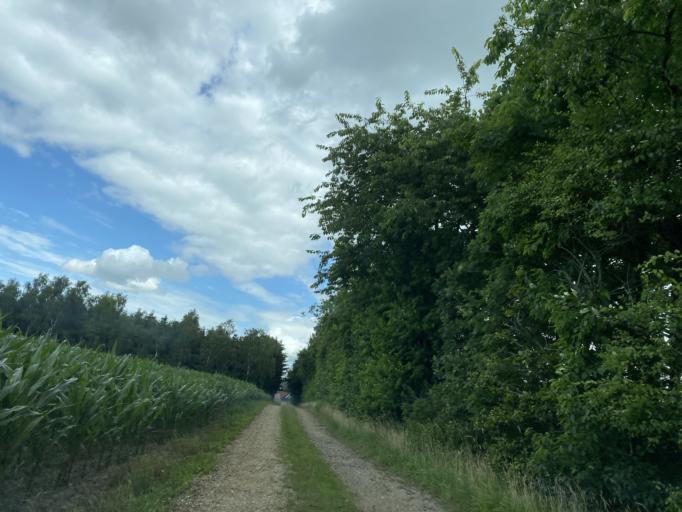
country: DK
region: Central Jutland
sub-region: Viborg Kommune
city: Bjerringbro
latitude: 56.2832
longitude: 9.6584
